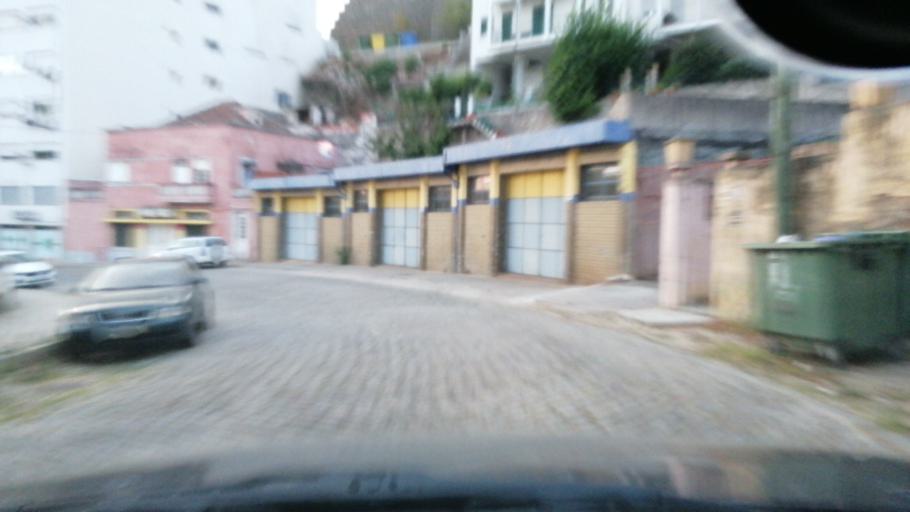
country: PT
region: Vila Real
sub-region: Peso da Regua
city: Peso da Regua
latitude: 41.1612
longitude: -7.7853
